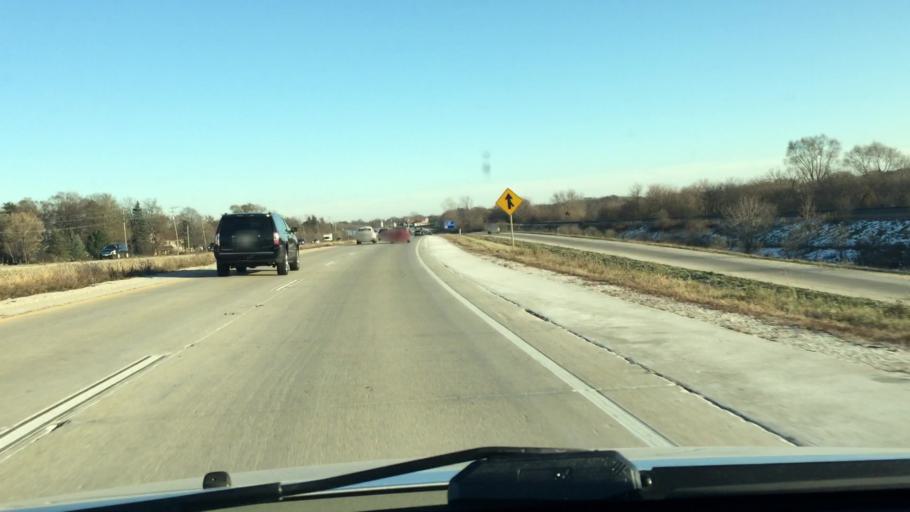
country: US
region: Wisconsin
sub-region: Waukesha County
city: Okauchee Lake
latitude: 43.1070
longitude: -88.4305
